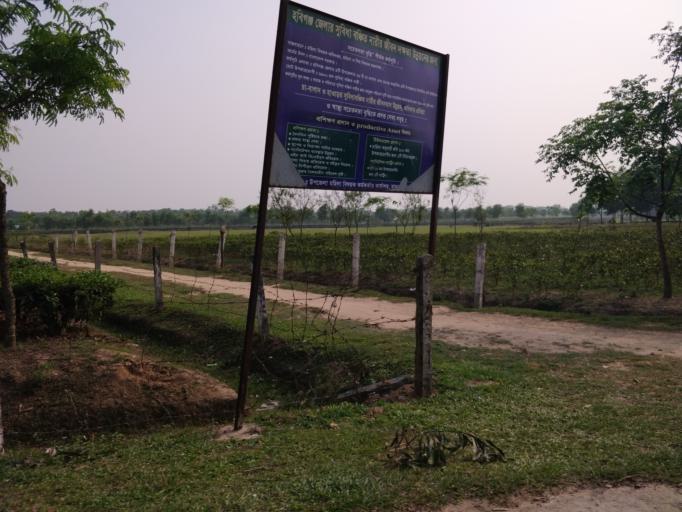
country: IN
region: Tripura
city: Khowai
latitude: 24.1293
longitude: 91.3785
